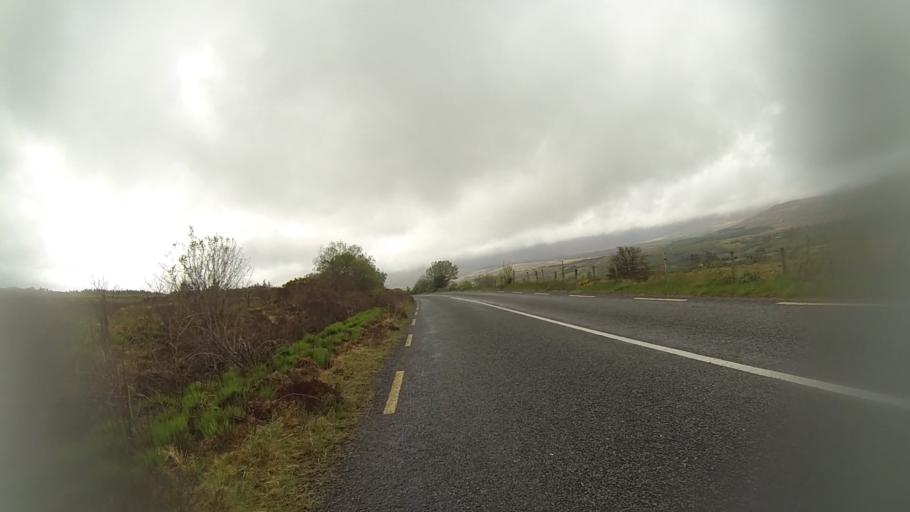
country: IE
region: Munster
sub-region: Ciarrai
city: Killorglin
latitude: 51.8557
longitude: -9.8661
